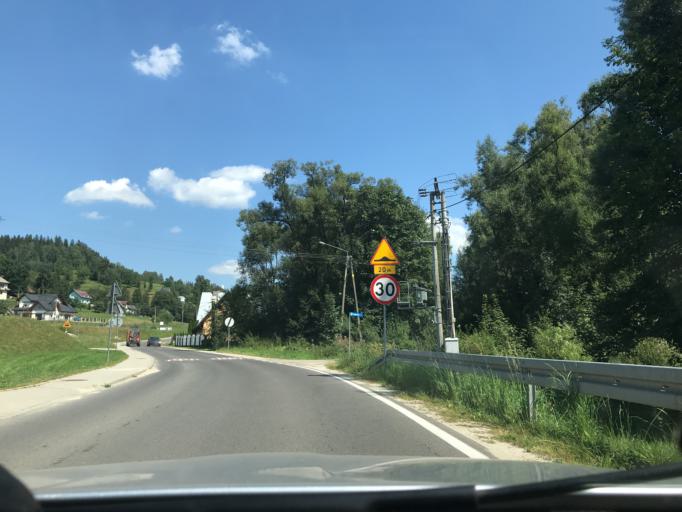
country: PL
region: Lesser Poland Voivodeship
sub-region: Powiat nowotarski
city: Sieniawa
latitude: 49.5378
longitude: 19.9388
